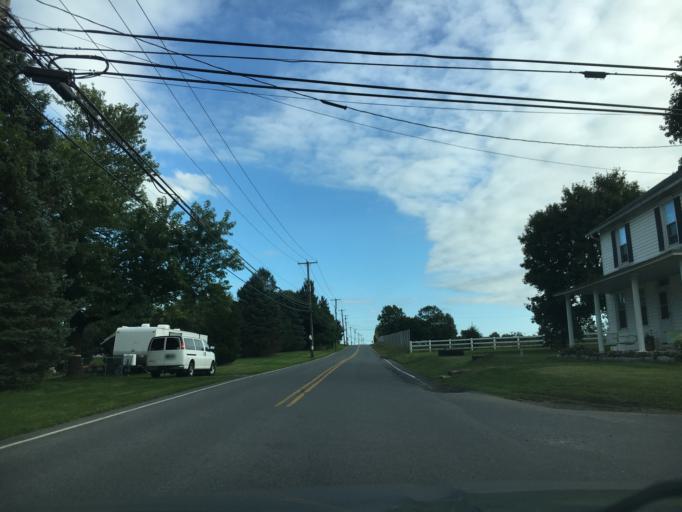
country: US
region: Pennsylvania
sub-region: Berks County
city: Topton
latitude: 40.5935
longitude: -75.7120
